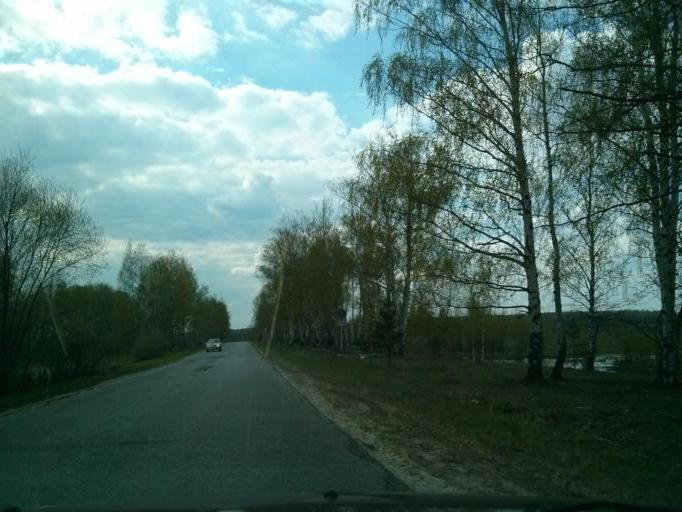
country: RU
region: Vladimir
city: Melenki
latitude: 55.3418
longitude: 41.8257
